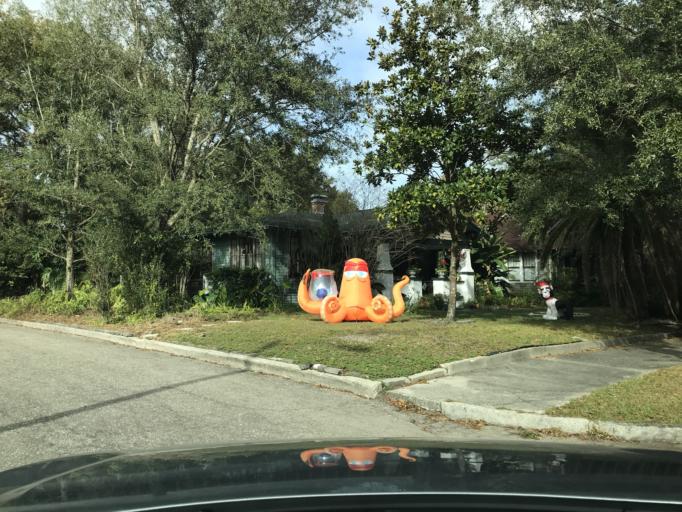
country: US
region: Florida
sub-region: Hillsborough County
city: Tampa
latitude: 27.9969
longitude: -82.4584
